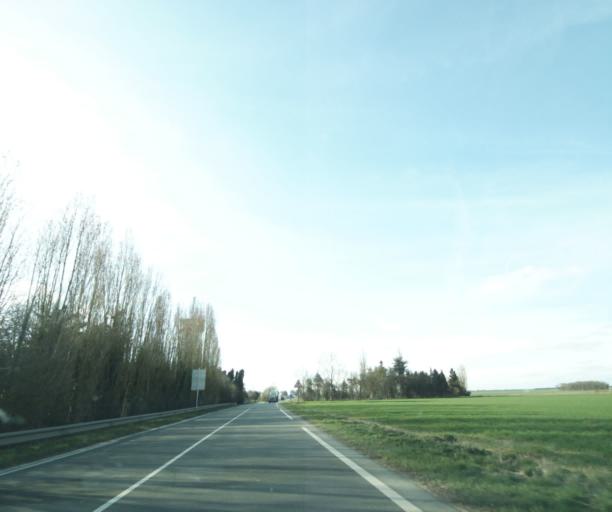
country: FR
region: Ile-de-France
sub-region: Departement des Yvelines
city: Ablis
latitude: 48.4643
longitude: 1.8798
